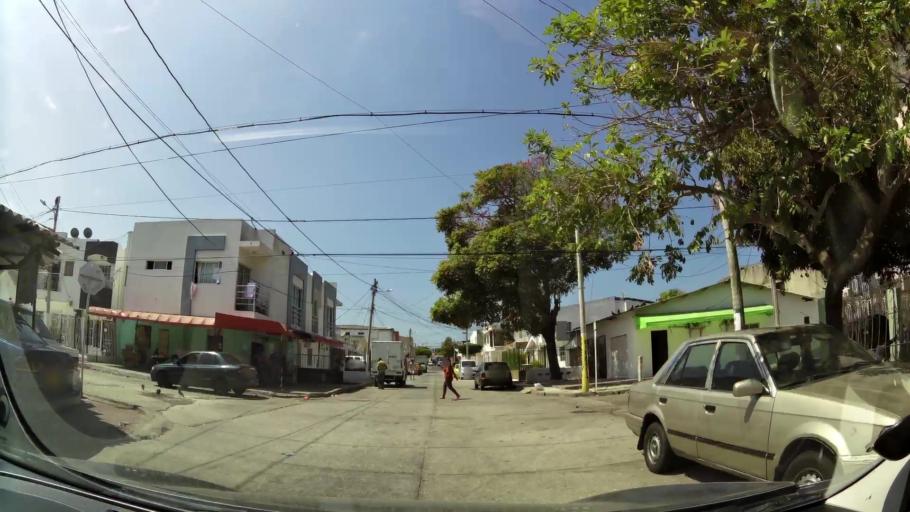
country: CO
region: Atlantico
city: Barranquilla
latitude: 10.9680
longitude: -74.8067
